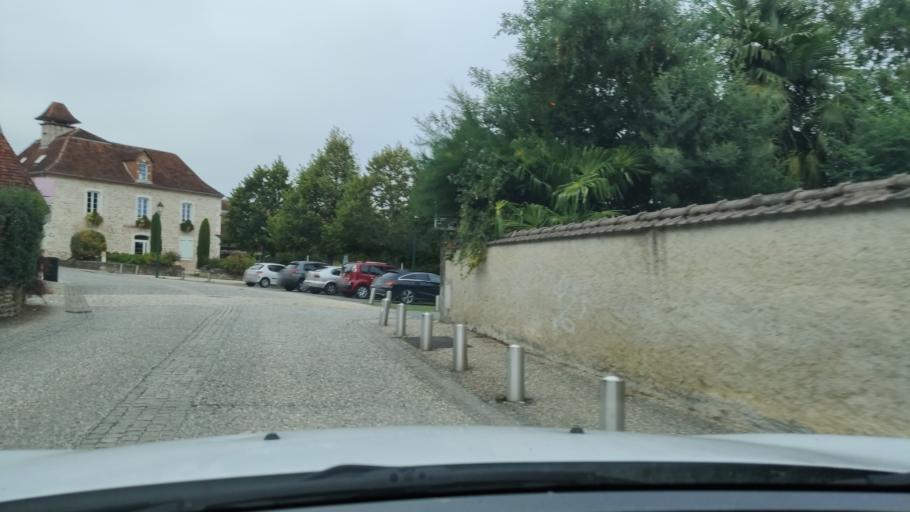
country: FR
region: Aquitaine
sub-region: Departement des Pyrenees-Atlantiques
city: Sauvagnon
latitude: 43.4034
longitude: -0.3868
